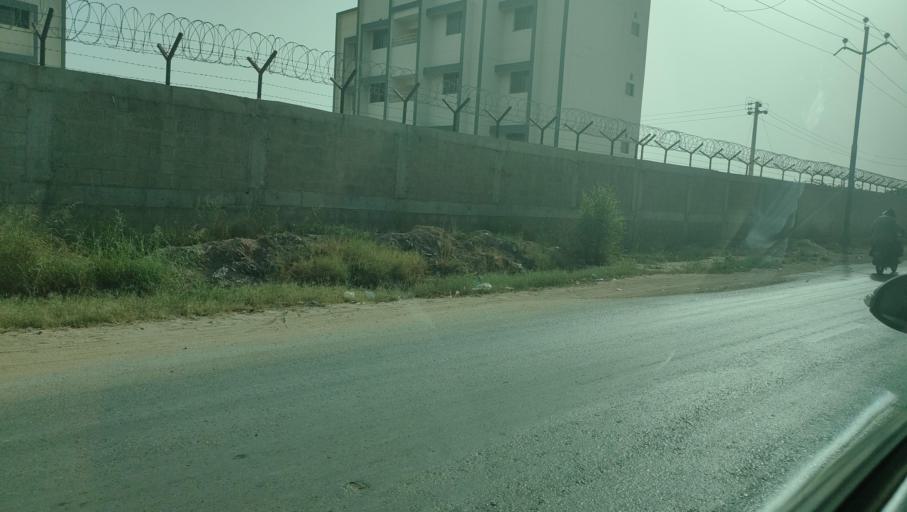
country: PK
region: Sindh
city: Malir Cantonment
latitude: 24.9234
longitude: 67.1822
